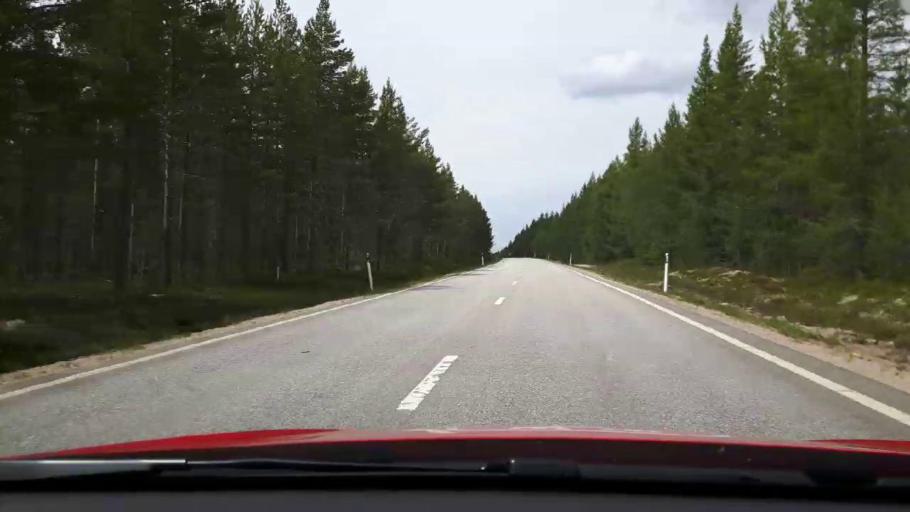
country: SE
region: Jaemtland
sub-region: Harjedalens Kommun
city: Sveg
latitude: 62.0588
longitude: 14.2932
